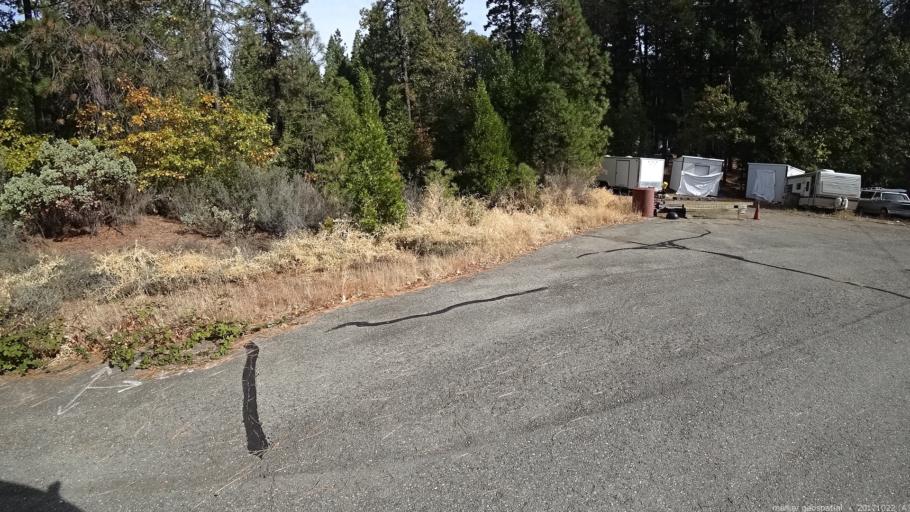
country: US
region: California
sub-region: Siskiyou County
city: Dunsmuir
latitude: 41.0569
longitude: -122.3760
